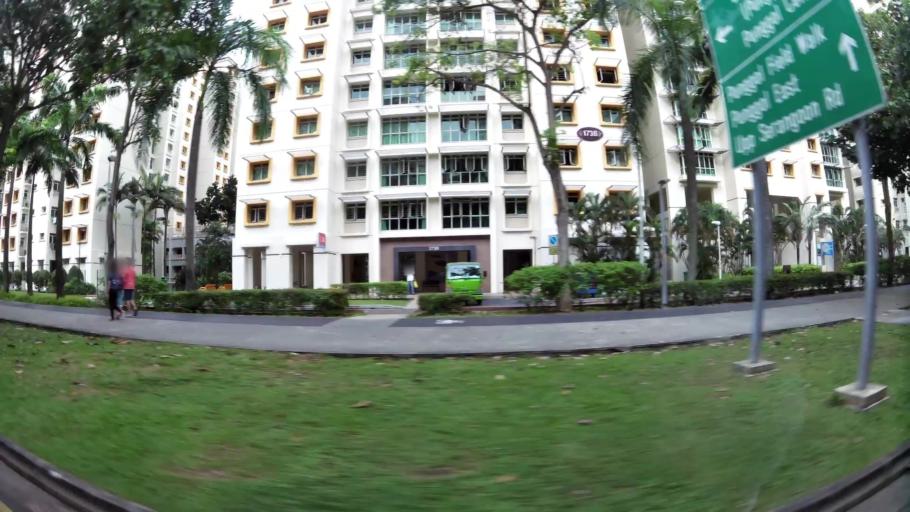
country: MY
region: Johor
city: Kampung Pasir Gudang Baru
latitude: 1.3964
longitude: 103.9099
